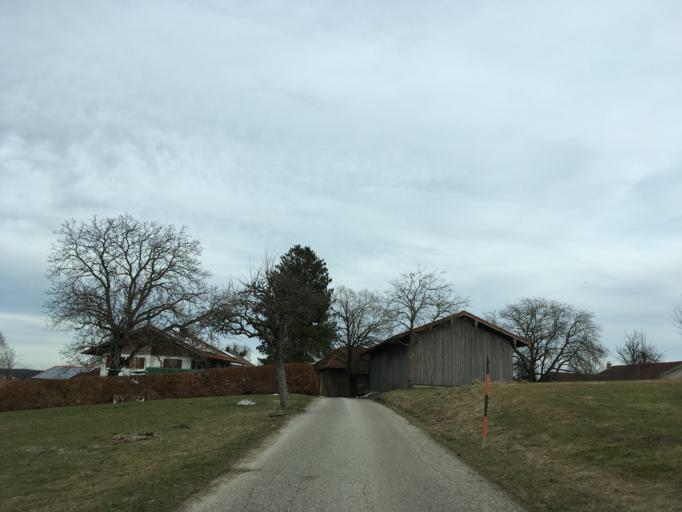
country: DE
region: Bavaria
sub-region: Upper Bavaria
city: Eggstatt
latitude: 47.9073
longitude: 12.3751
